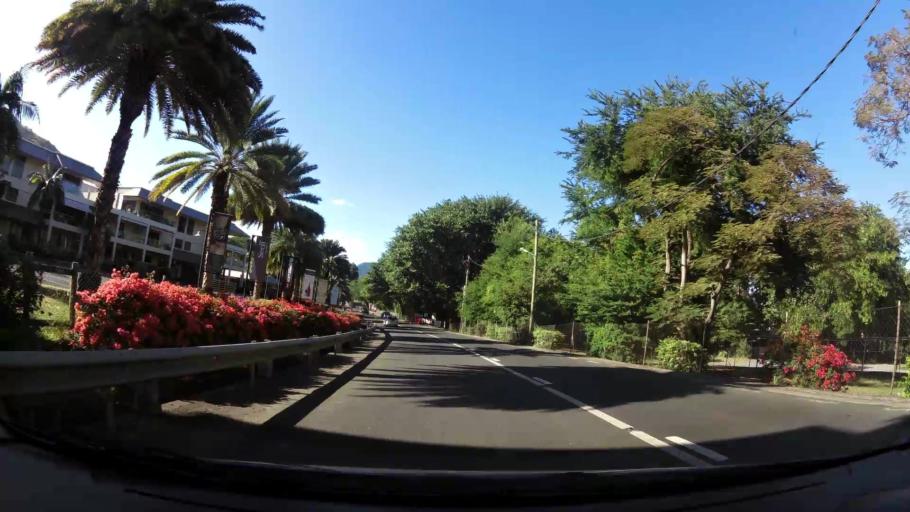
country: MU
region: Black River
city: Grande Riviere Noire
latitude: -20.3582
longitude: 57.3682
